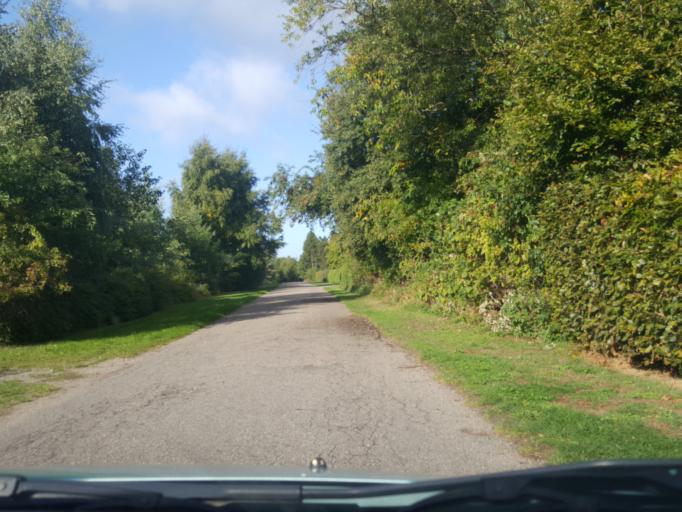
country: DK
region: Zealand
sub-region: Guldborgsund Kommune
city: Nykobing Falster
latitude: 54.6537
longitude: 11.9538
